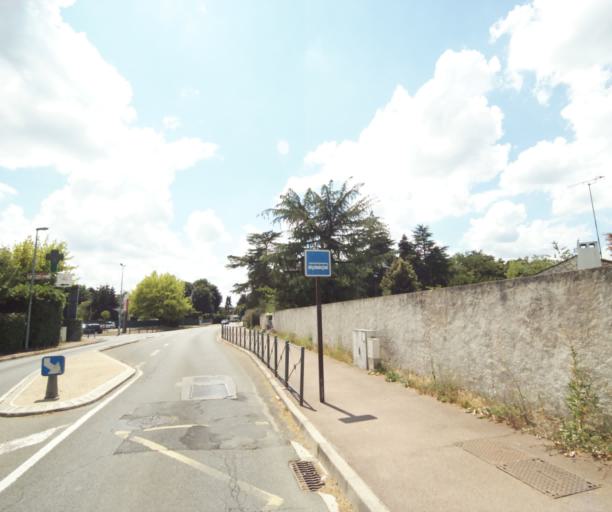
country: FR
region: Ile-de-France
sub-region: Departement de Seine-et-Marne
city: Samoreau
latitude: 48.4339
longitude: 2.7523
